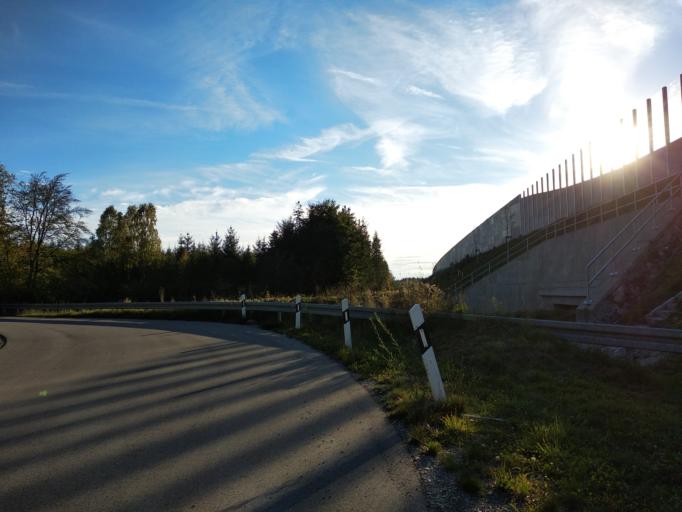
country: DE
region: Bavaria
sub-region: Upper Bavaria
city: Hohenbrunn
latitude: 48.0358
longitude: 11.6761
